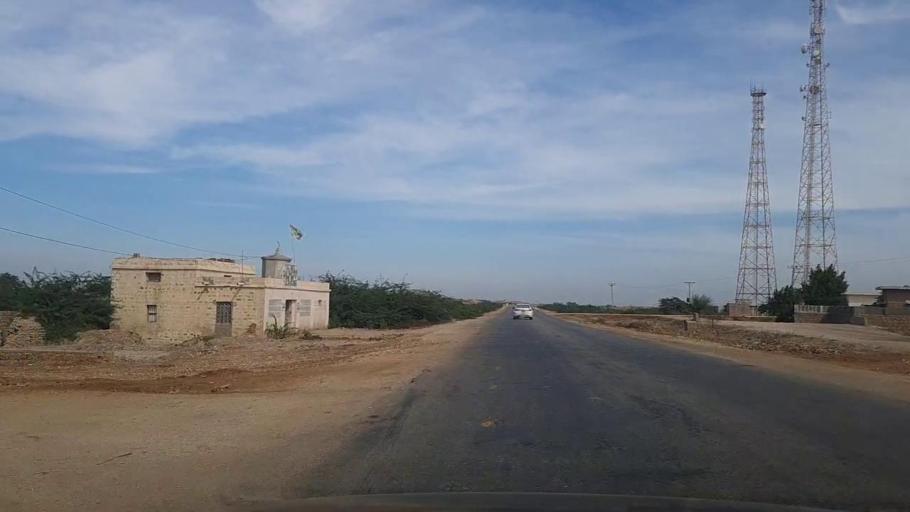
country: PK
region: Sindh
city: Daro Mehar
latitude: 24.8982
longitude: 68.0646
